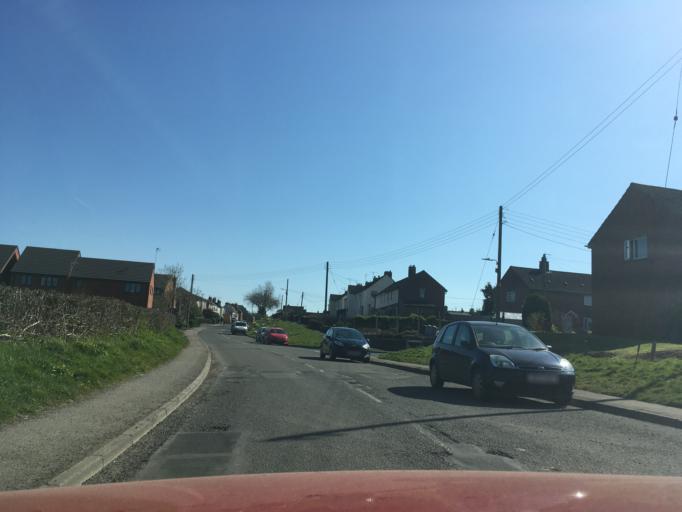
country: GB
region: England
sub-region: Gloucestershire
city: Berkeley
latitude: 51.6921
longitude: -2.4665
